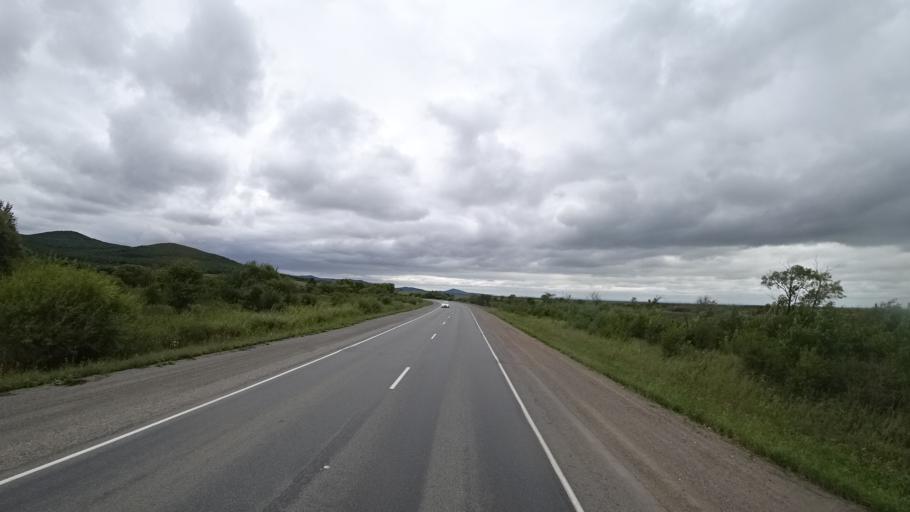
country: RU
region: Primorskiy
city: Chernigovka
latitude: 44.3122
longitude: 132.5493
